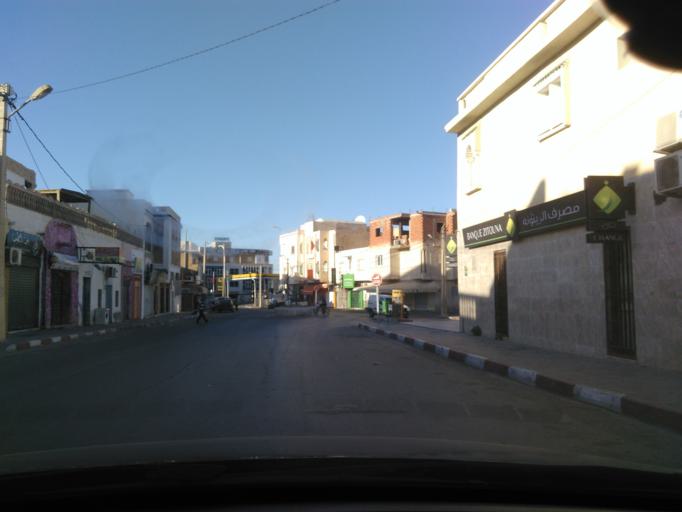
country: TN
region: Tataouine
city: Tataouine
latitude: 32.9306
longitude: 10.4499
